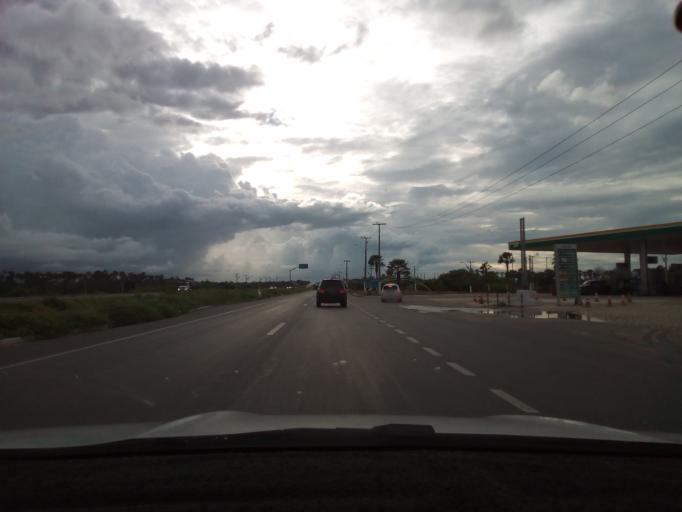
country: BR
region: Ceara
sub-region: Aracati
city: Aracati
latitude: -4.5790
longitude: -37.7787
